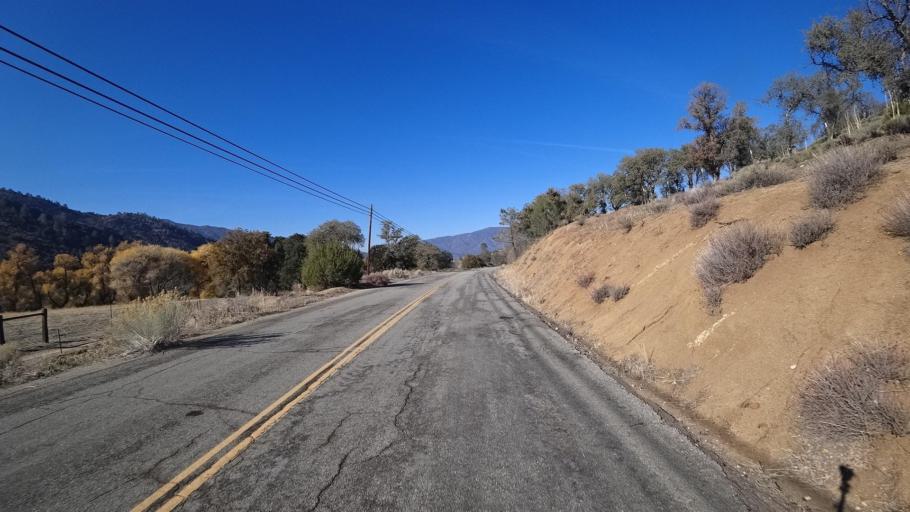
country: US
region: California
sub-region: Kern County
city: Bodfish
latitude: 35.3970
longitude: -118.4503
